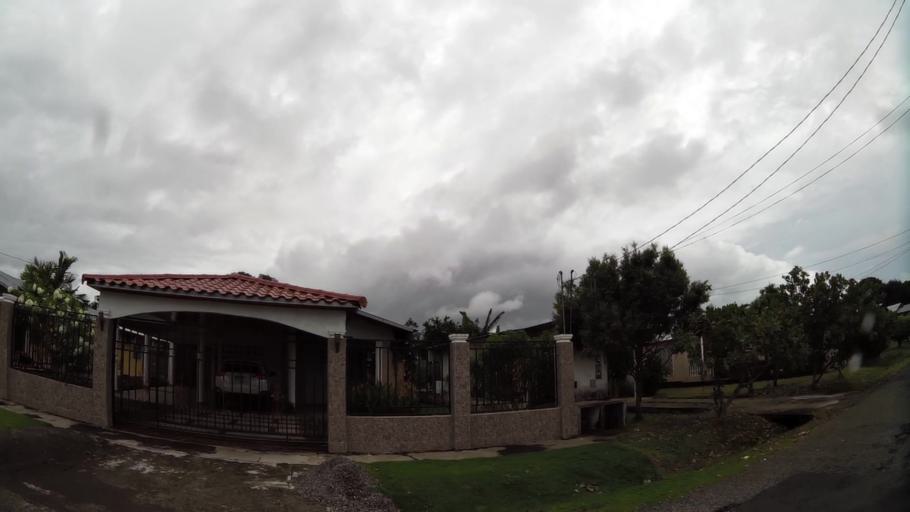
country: PA
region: Chiriqui
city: David
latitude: 8.4021
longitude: -82.4607
